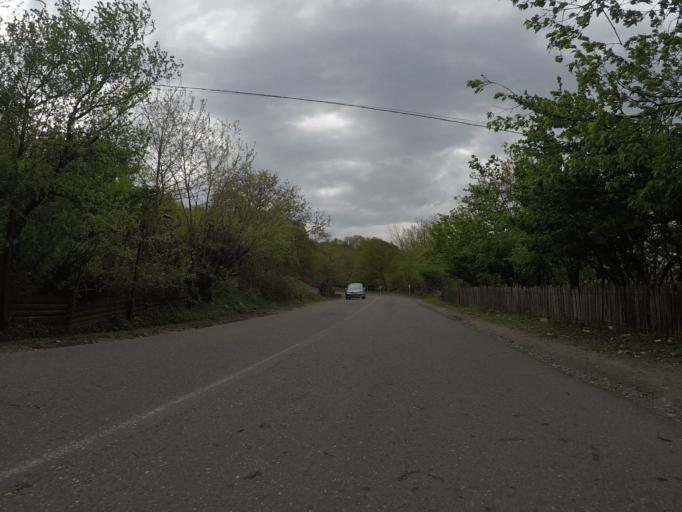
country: GE
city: Tqibuli
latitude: 42.2804
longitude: 43.2056
